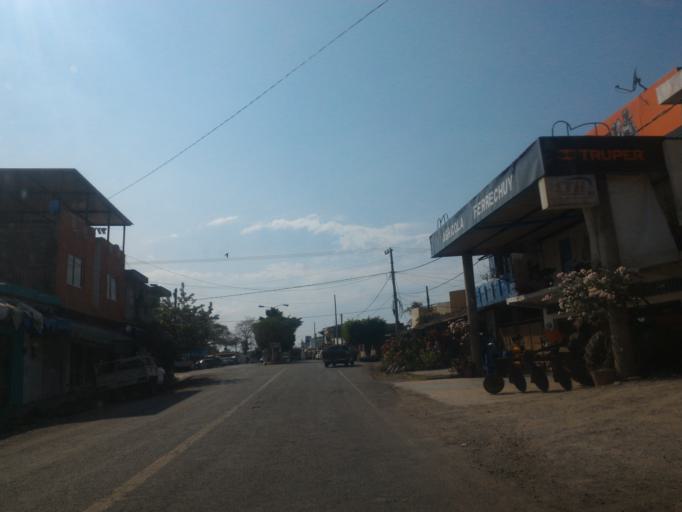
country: MX
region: Michoacan
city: Coahuayana Viejo
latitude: 18.5319
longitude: -103.5910
